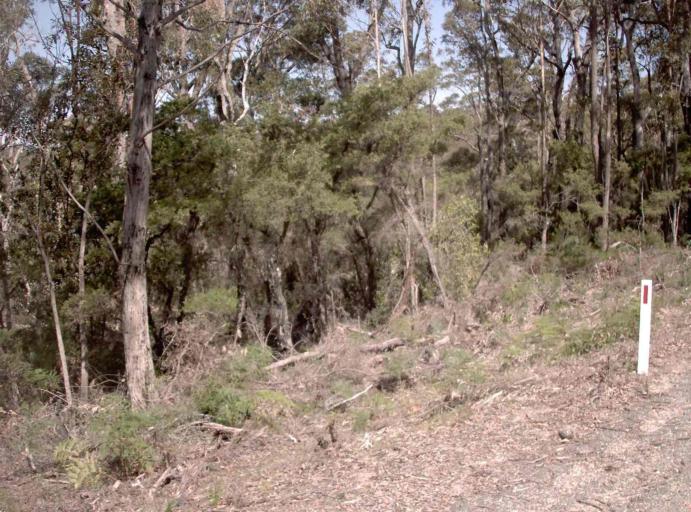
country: AU
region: New South Wales
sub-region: Bega Valley
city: Eden
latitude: -37.5422
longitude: 149.6975
